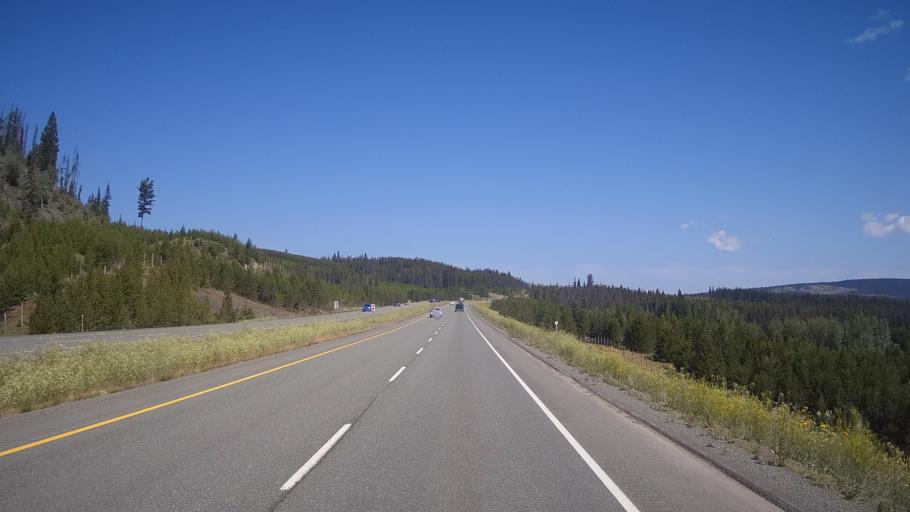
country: CA
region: British Columbia
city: Logan Lake
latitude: 50.3625
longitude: -120.6272
